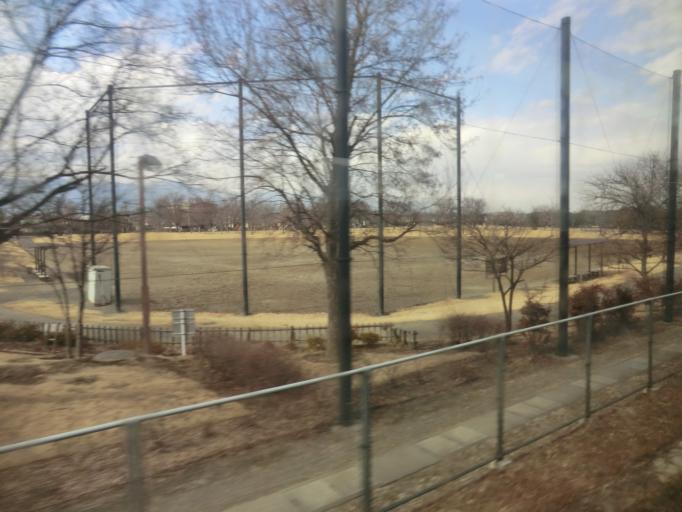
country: JP
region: Nagano
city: Matsumoto
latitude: 36.1832
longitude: 137.9593
